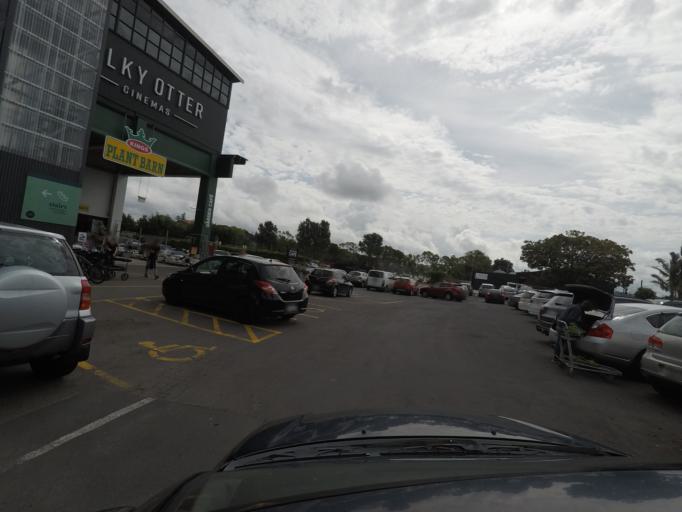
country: NZ
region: Auckland
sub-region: Auckland
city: Auckland
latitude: -36.8627
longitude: 174.8093
